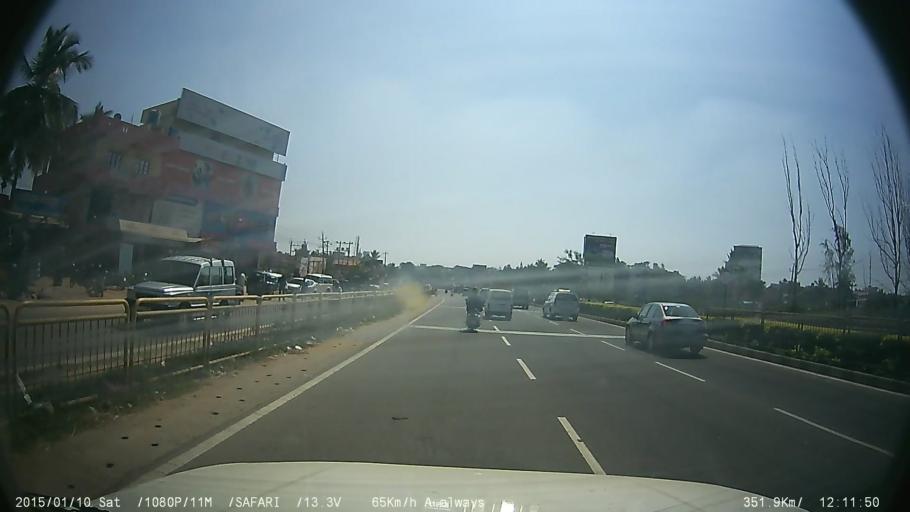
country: IN
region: Karnataka
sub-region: Bangalore Urban
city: Anekal
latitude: 12.8288
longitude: 77.6818
